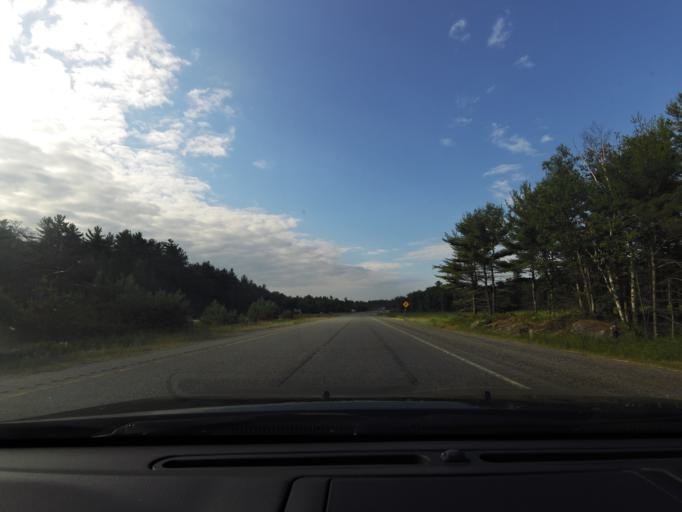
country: CA
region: Ontario
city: Gravenhurst
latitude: 44.9215
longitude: -79.3431
